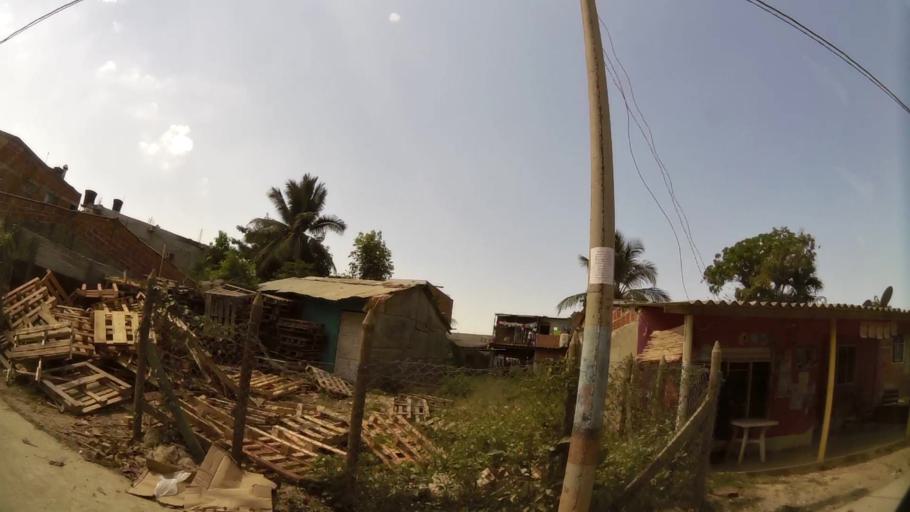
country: CO
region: Bolivar
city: Cartagena
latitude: 10.3455
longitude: -75.4869
